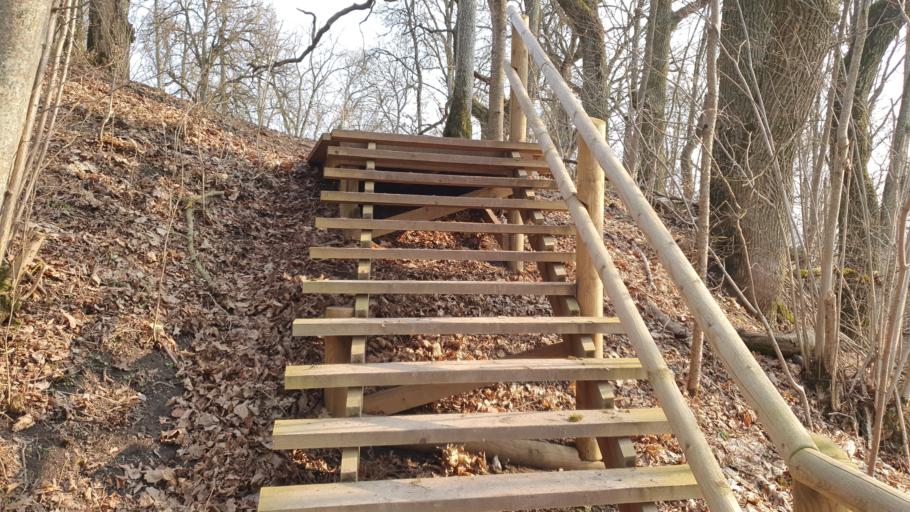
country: LV
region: Rundales
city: Pilsrundale
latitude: 56.4356
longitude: 24.0426
